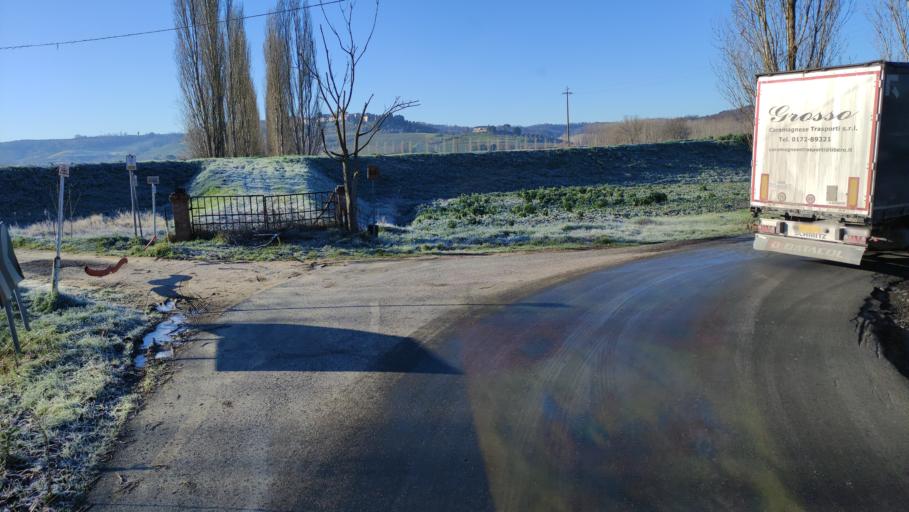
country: IT
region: Tuscany
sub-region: Province of Florence
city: Castelfiorentino
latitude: 43.6467
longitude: 10.9465
